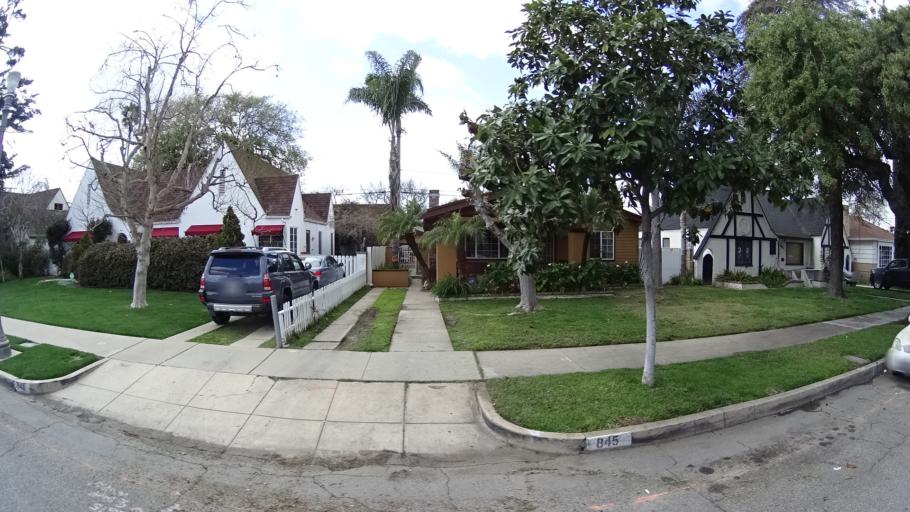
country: US
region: California
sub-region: Orange County
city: Anaheim
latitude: 33.8452
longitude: -117.9202
